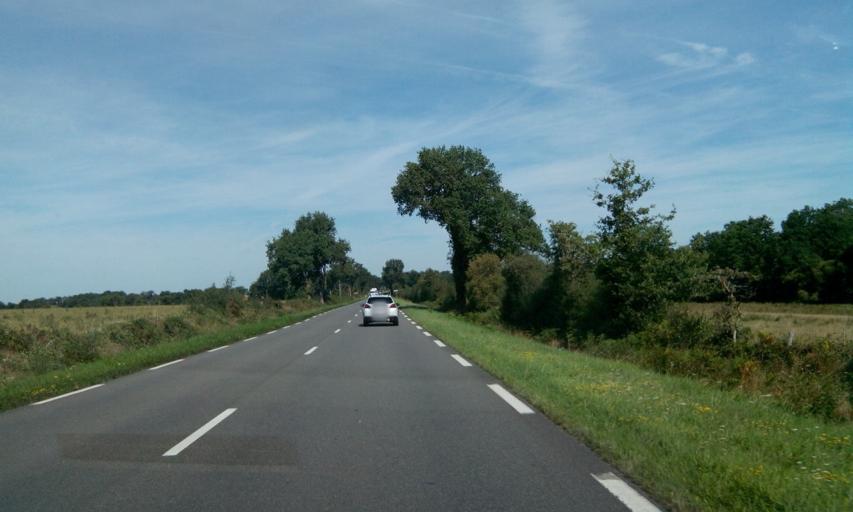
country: FR
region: Poitou-Charentes
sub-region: Departement de la Vienne
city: Availles-Limouzine
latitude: 46.0661
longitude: 0.5993
